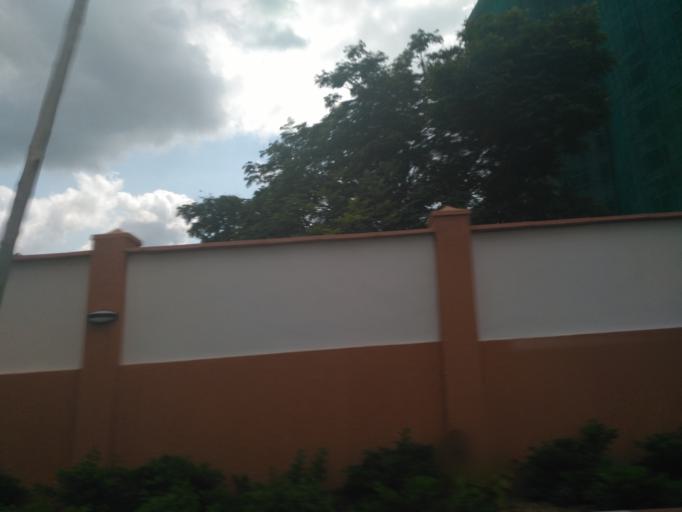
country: TZ
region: Dar es Salaam
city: Dar es Salaam
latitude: -6.7998
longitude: 39.2871
